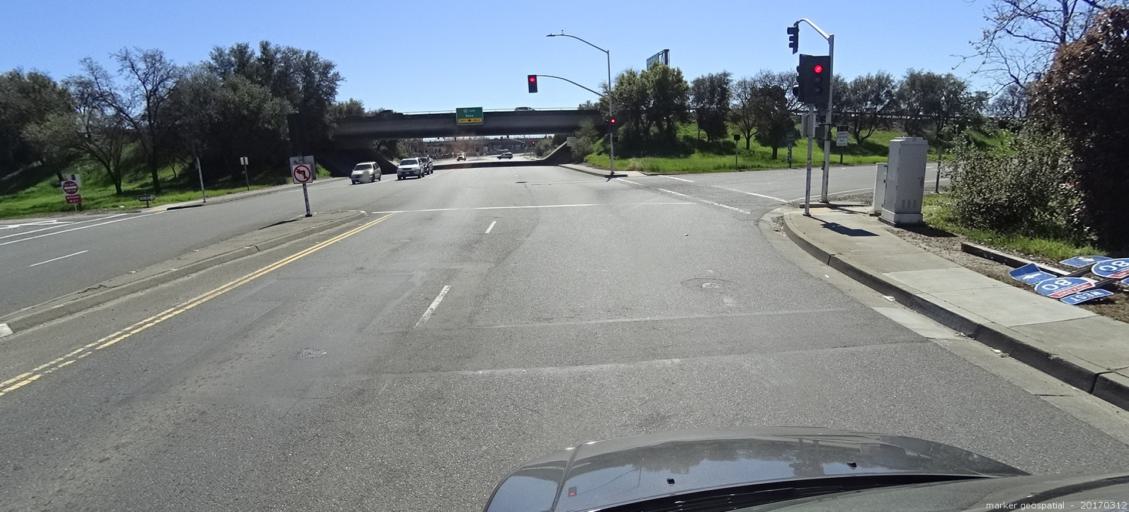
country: US
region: California
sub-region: Sacramento County
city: Arden-Arcade
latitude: 38.6383
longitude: -121.4115
